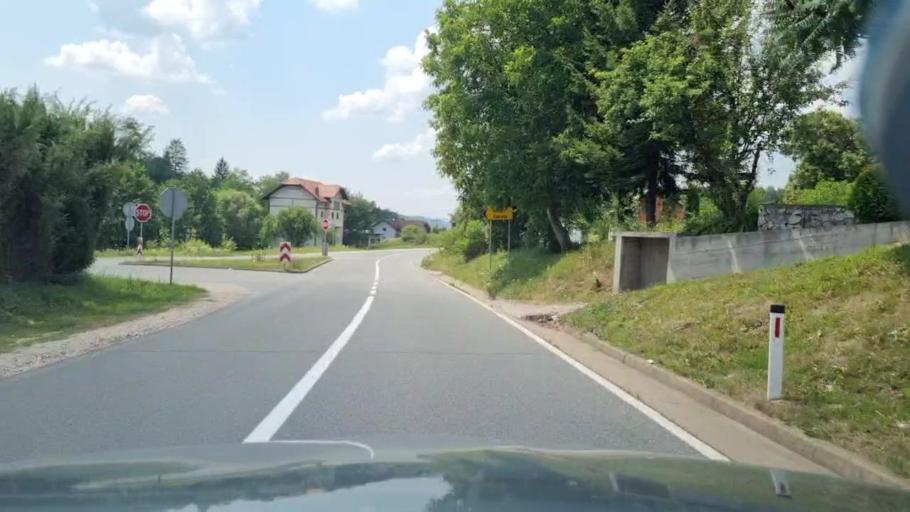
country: BA
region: Federation of Bosnia and Herzegovina
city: Tojsici
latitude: 44.5319
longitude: 18.7833
